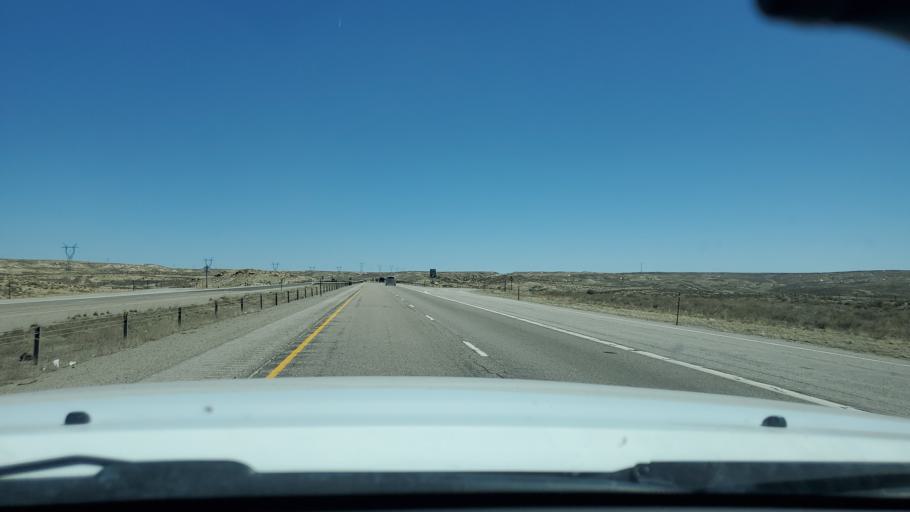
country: US
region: Wyoming
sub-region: Sweetwater County
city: Rock Springs
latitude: 41.6481
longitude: -108.6301
